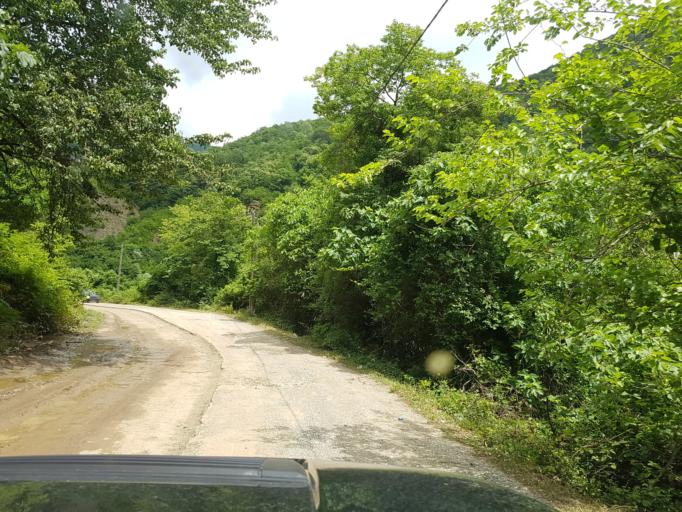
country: GE
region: Imereti
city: Kutaisi
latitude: 42.4379
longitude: 42.7573
